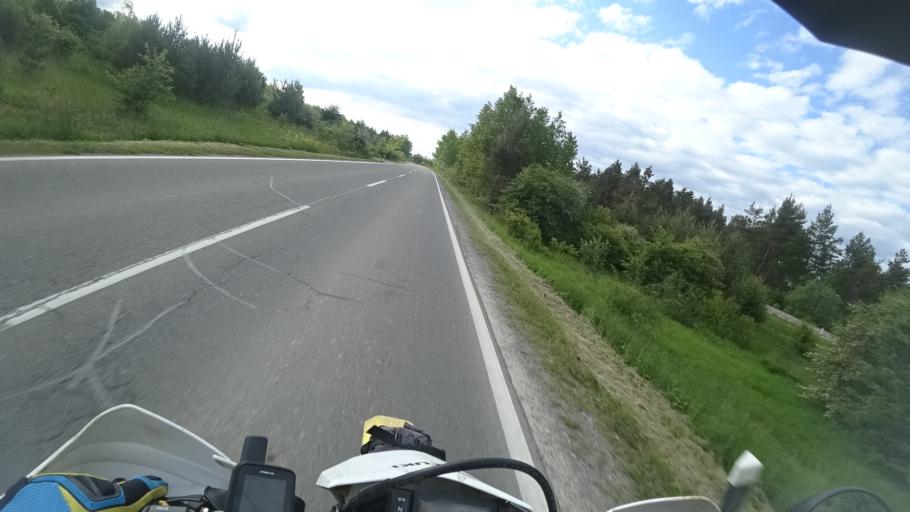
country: HR
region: Licko-Senjska
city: Gospic
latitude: 44.5244
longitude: 15.4123
